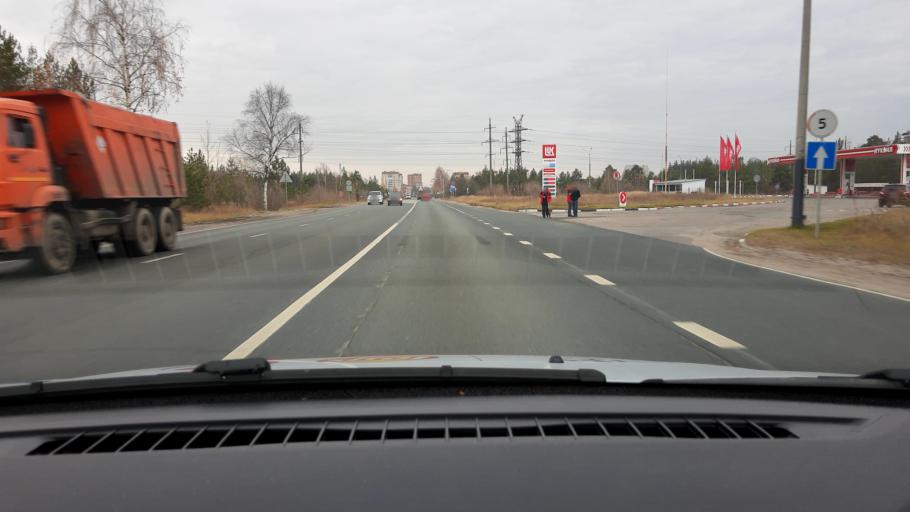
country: RU
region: Nizjnij Novgorod
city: Dzerzhinsk
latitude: 56.2629
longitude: 43.4690
